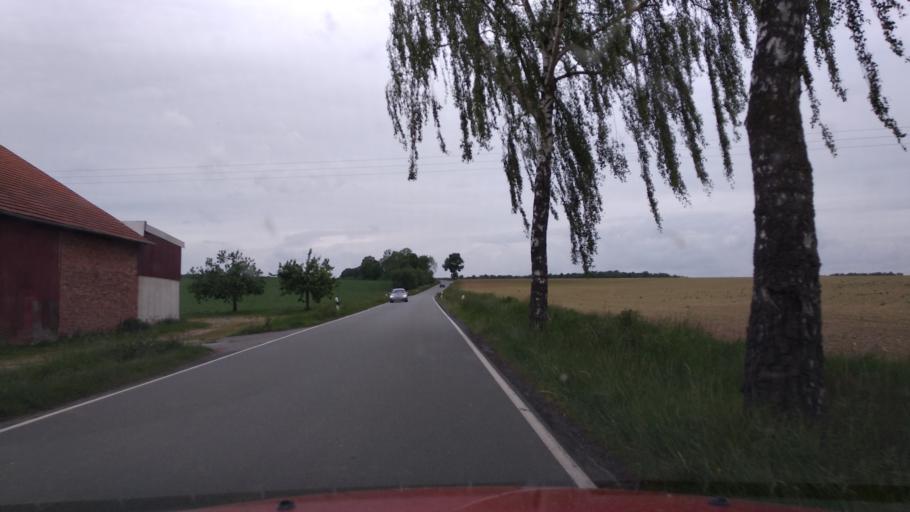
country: DE
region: North Rhine-Westphalia
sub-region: Regierungsbezirk Detmold
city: Willebadessen
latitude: 51.6062
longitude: 9.1208
